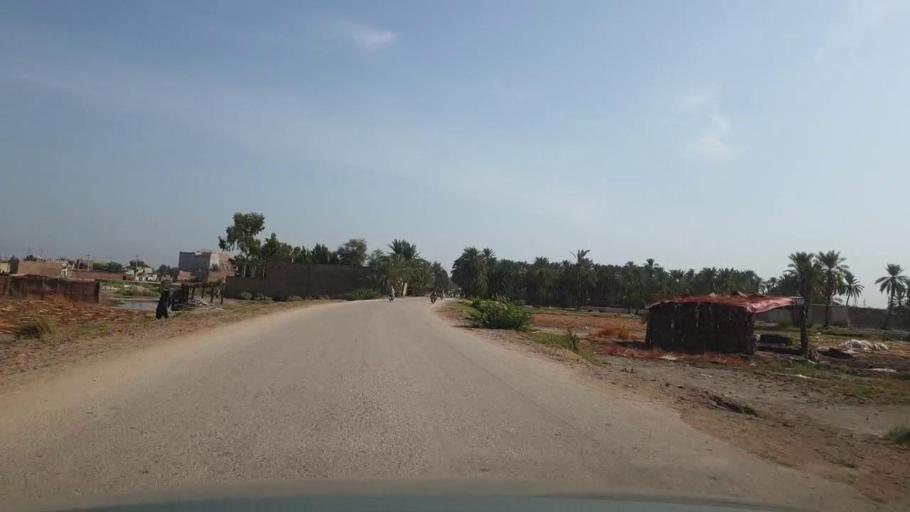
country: PK
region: Sindh
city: Rohri
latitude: 27.6731
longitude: 68.8798
